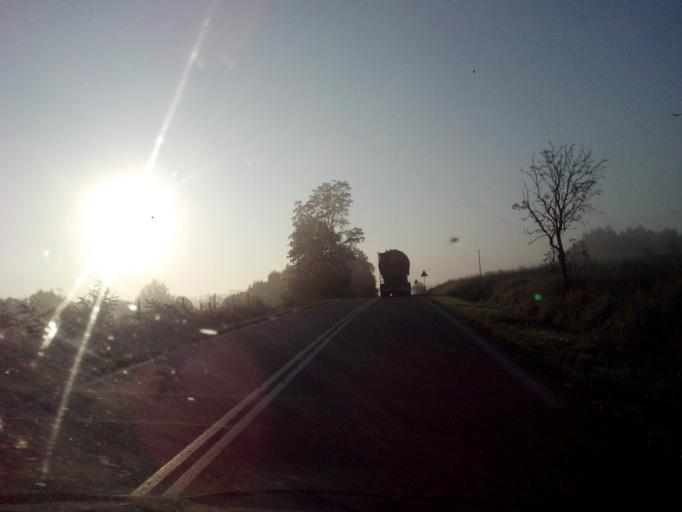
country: PL
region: Subcarpathian Voivodeship
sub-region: Powiat strzyzowski
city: Gwoznica Gorna
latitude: 49.8135
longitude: 21.9975
